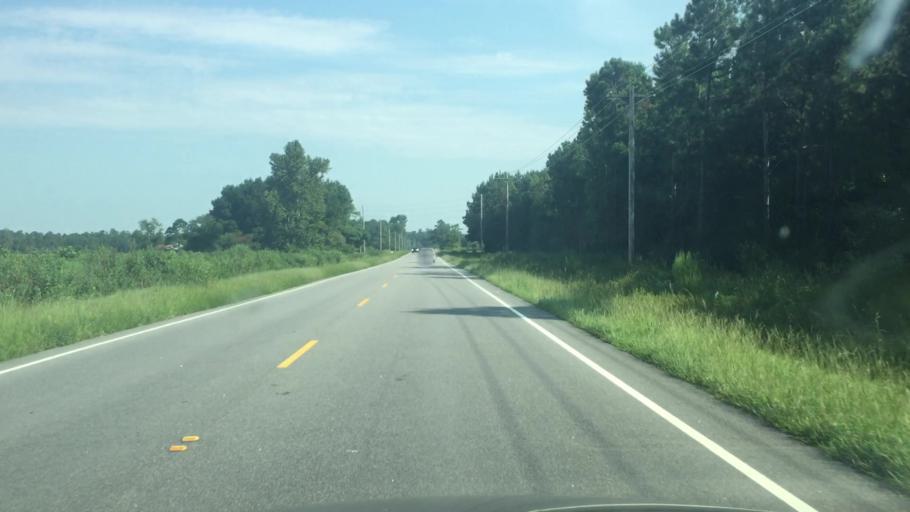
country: US
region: North Carolina
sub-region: Columbus County
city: Tabor City
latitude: 34.2232
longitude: -78.8241
